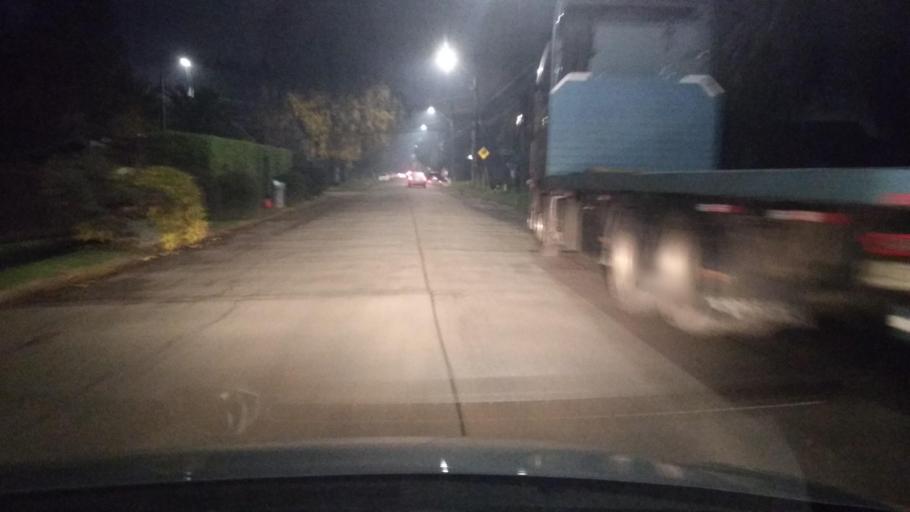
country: CL
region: Los Rios
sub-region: Provincia de Valdivia
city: Valdivia
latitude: -39.8154
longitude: -73.2574
